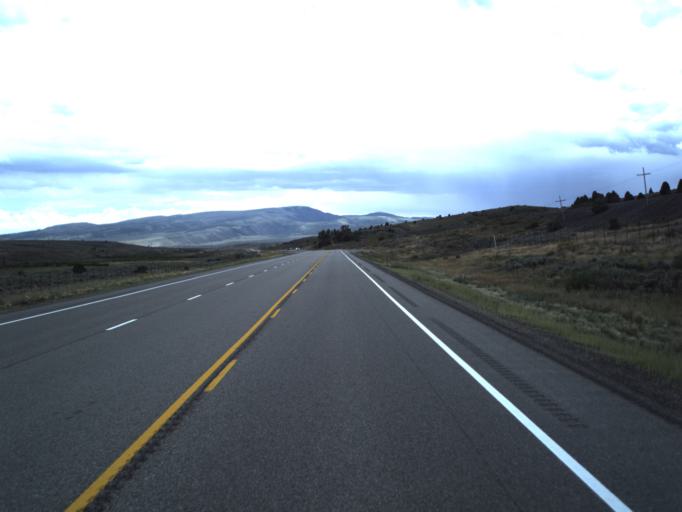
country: US
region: Utah
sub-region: Carbon County
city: Helper
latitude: 39.9096
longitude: -111.0611
